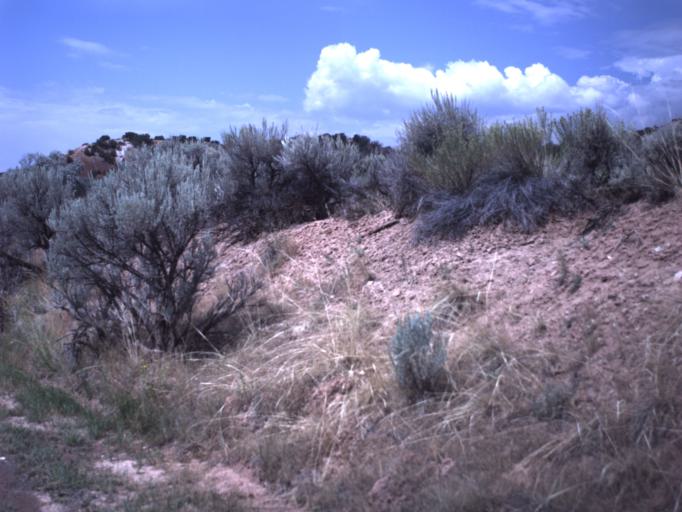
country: US
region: Utah
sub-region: Uintah County
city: Maeser
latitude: 40.5220
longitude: -109.5386
